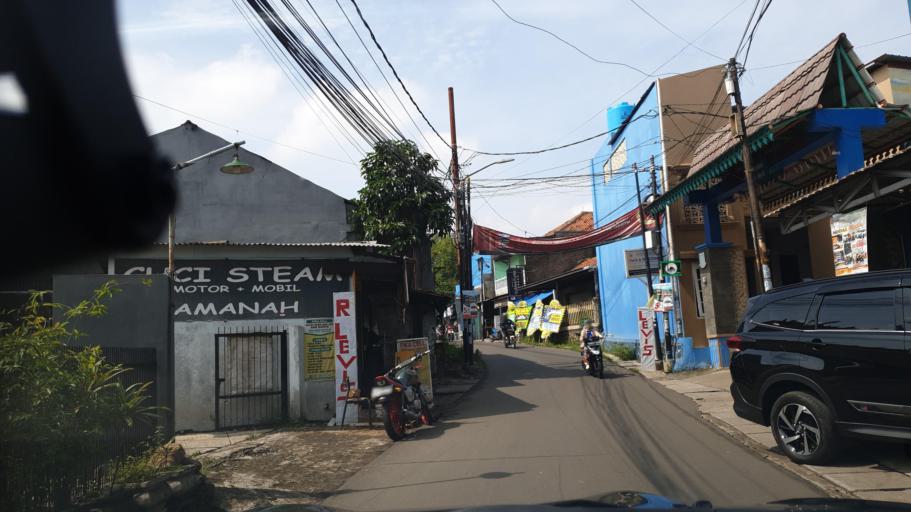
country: ID
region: West Java
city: Pamulang
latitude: -6.3193
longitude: 106.7551
